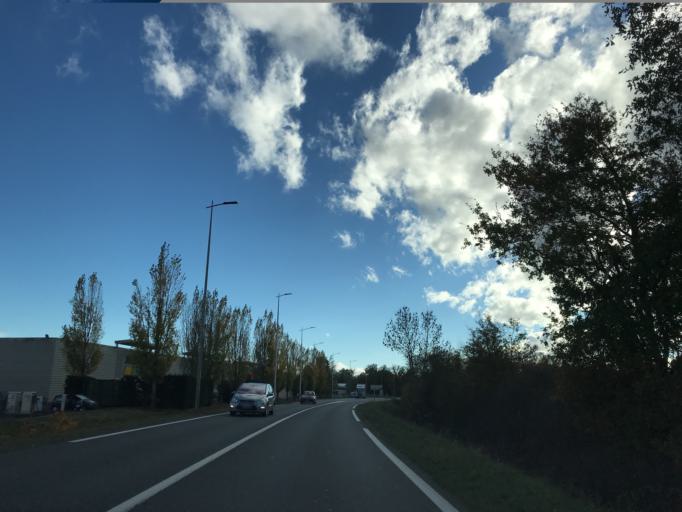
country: FR
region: Auvergne
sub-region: Departement du Puy-de-Dome
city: Peschadoires
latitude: 45.8384
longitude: 3.5065
